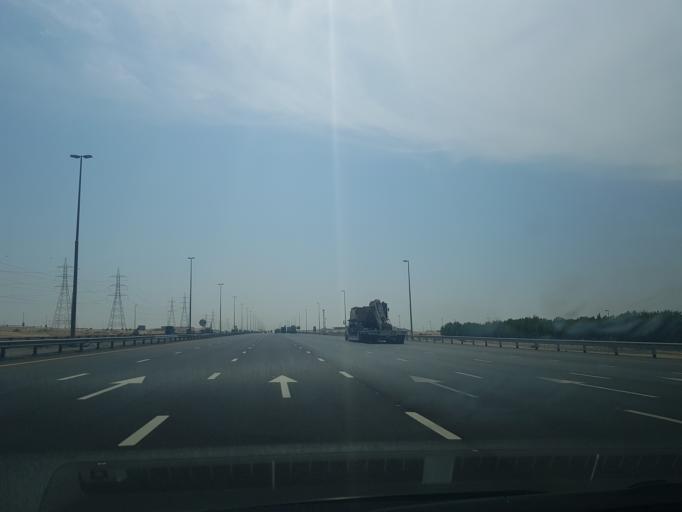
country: AE
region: Ash Shariqah
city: Sharjah
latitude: 25.2638
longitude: 55.5778
